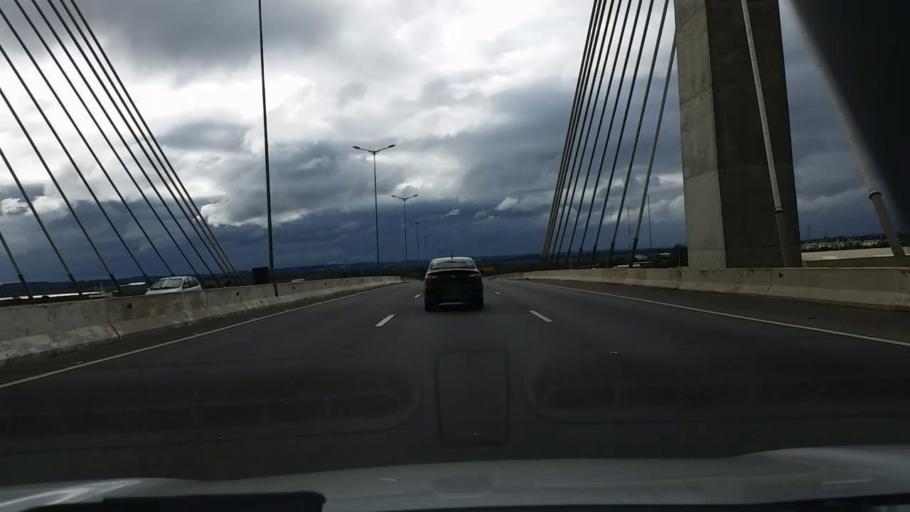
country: BR
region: Rio Grande do Sul
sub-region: Canoas
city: Canoas
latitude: -29.9710
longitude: -51.1999
